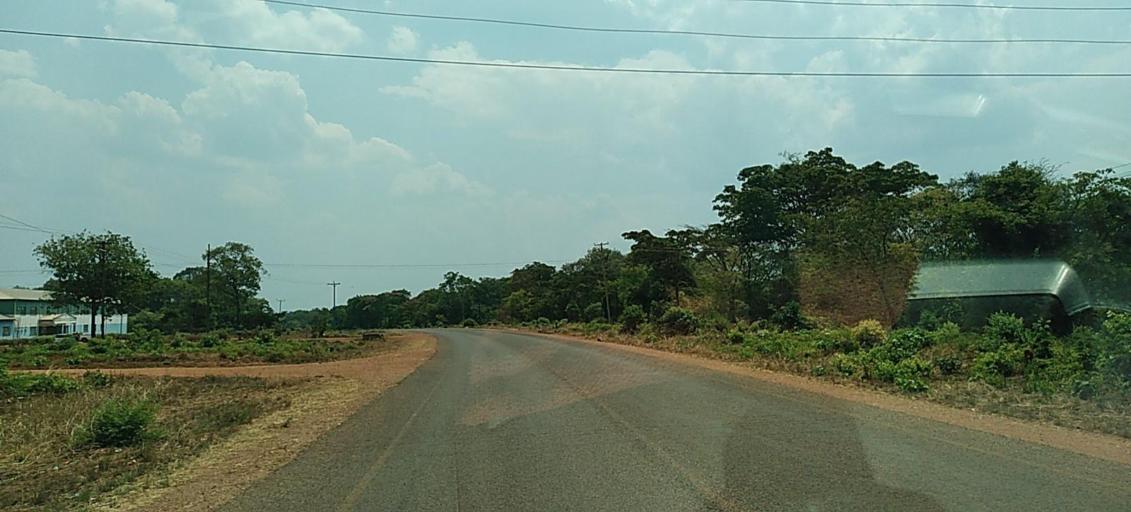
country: ZM
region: Copperbelt
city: Chingola
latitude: -12.8574
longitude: 27.6210
